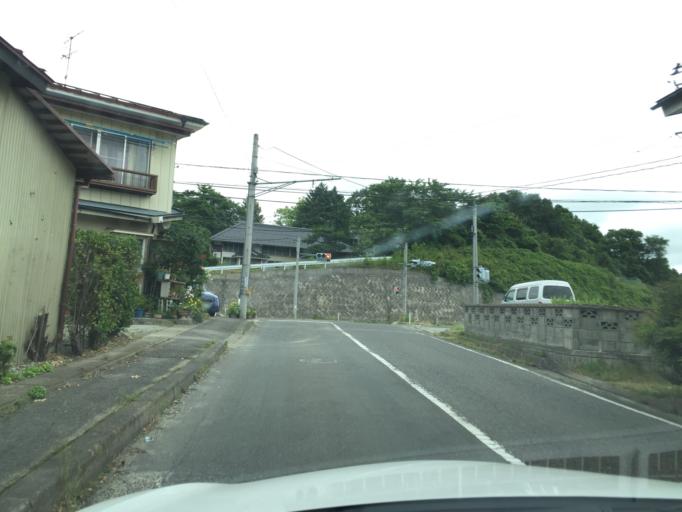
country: JP
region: Fukushima
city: Funehikimachi-funehiki
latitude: 37.4359
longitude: 140.5519
